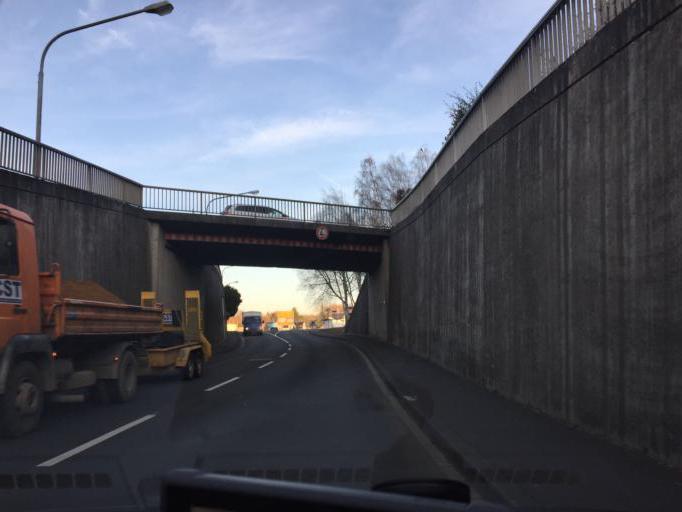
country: DE
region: Rheinland-Pfalz
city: Montabaur
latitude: 50.4404
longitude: 7.8230
